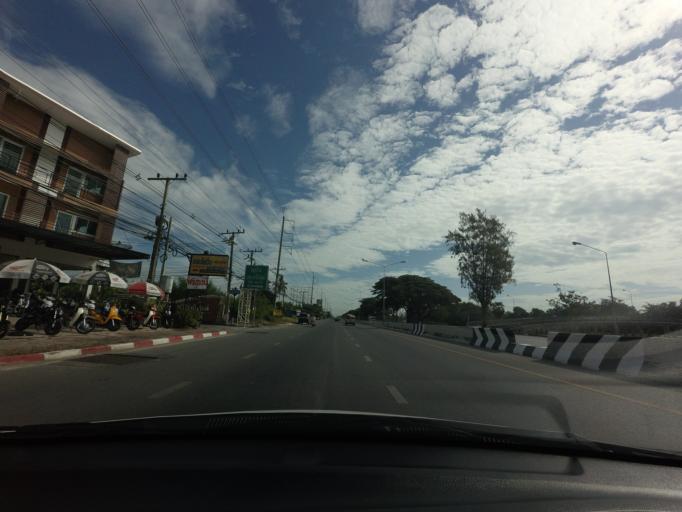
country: TH
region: Pathum Thani
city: Nong Suea
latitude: 14.0663
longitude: 100.8626
